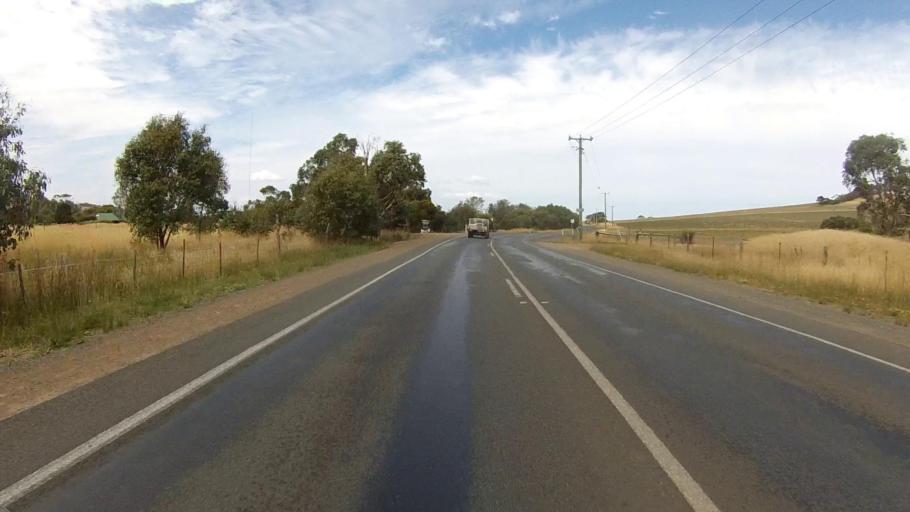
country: AU
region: Tasmania
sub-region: Clarence
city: Sandford
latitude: -42.9471
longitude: 147.5016
